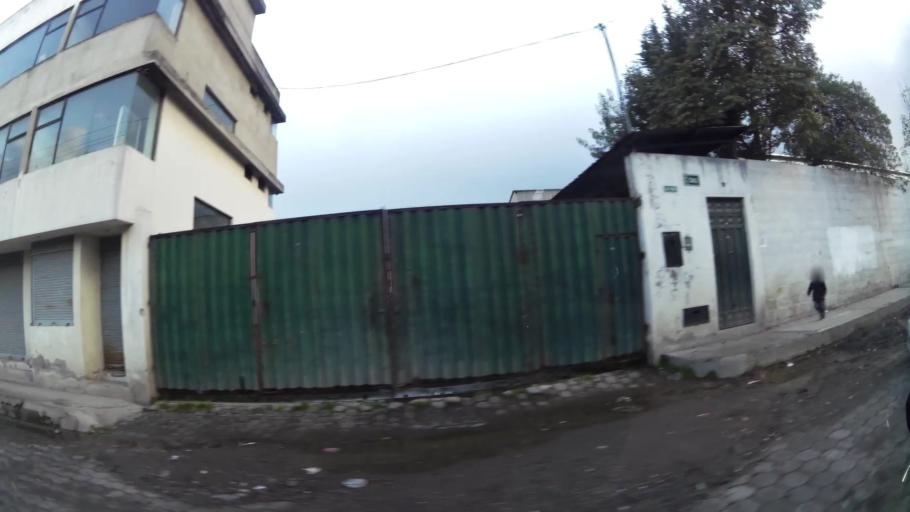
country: EC
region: Pichincha
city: Quito
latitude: -0.3082
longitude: -78.5427
